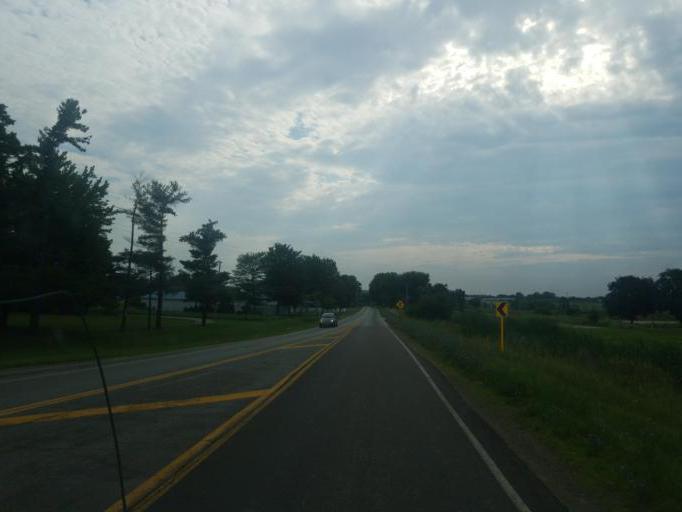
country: US
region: Ohio
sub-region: Wayne County
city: Orrville
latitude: 40.7949
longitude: -81.7897
